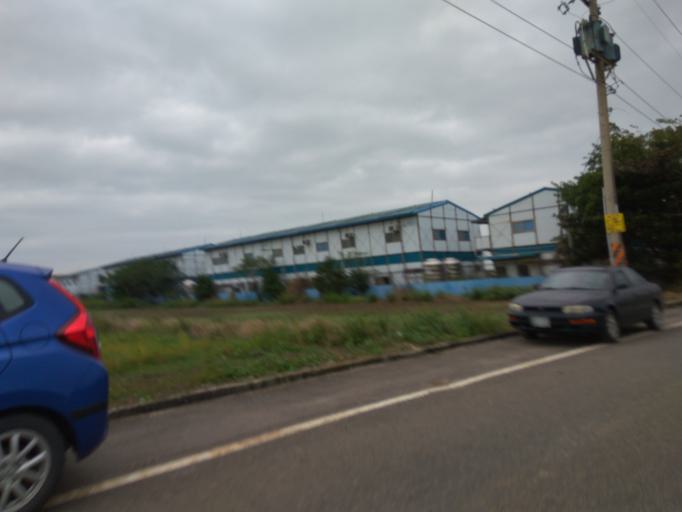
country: TW
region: Taiwan
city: Taoyuan City
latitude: 25.0287
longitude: 121.2217
